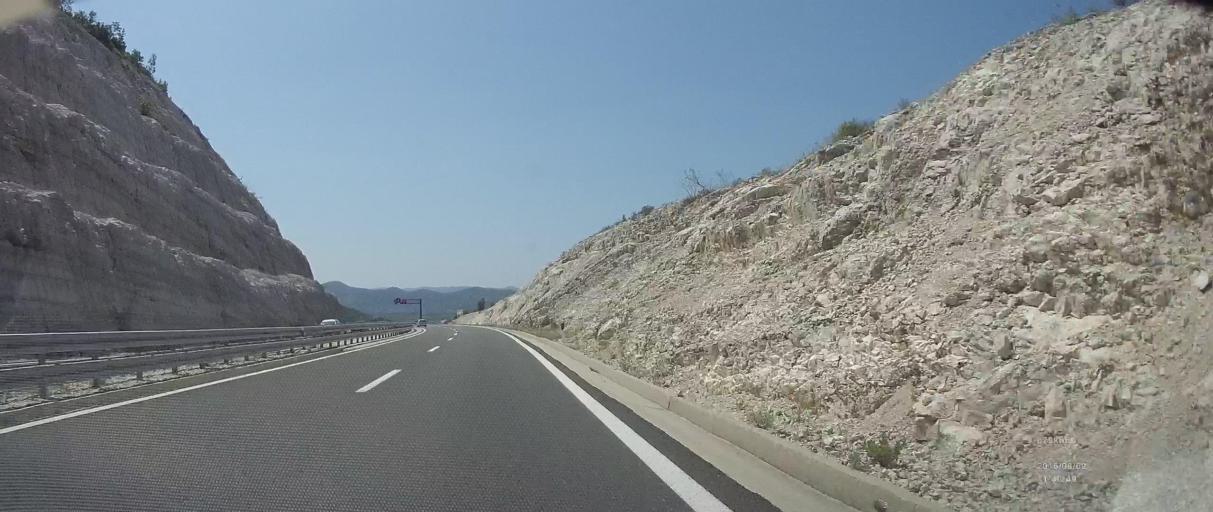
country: HR
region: Dubrovacko-Neretvanska
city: Komin
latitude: 43.0705
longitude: 17.4931
